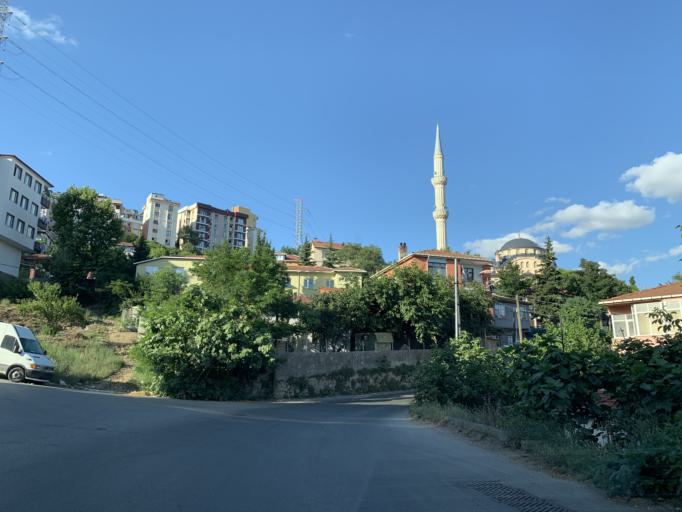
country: TR
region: Istanbul
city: Pendik
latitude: 40.9017
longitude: 29.2566
